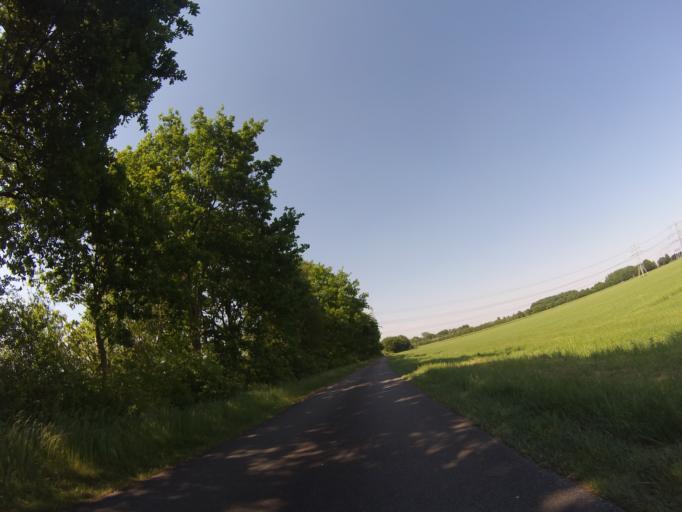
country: NL
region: Drenthe
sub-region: Gemeente Coevorden
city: Sleen
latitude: 52.7206
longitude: 6.8028
